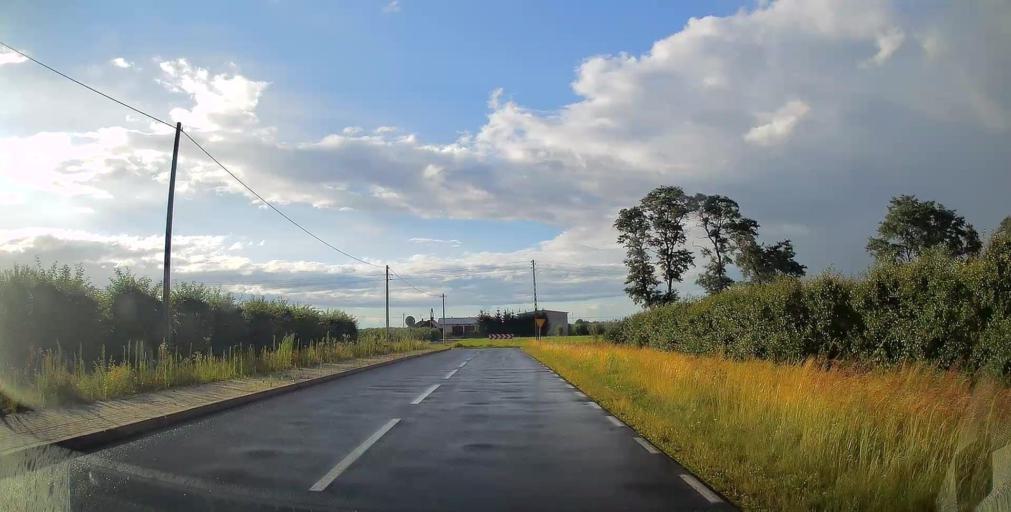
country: PL
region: Masovian Voivodeship
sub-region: Powiat grojecki
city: Goszczyn
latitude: 51.7634
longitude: 20.8990
